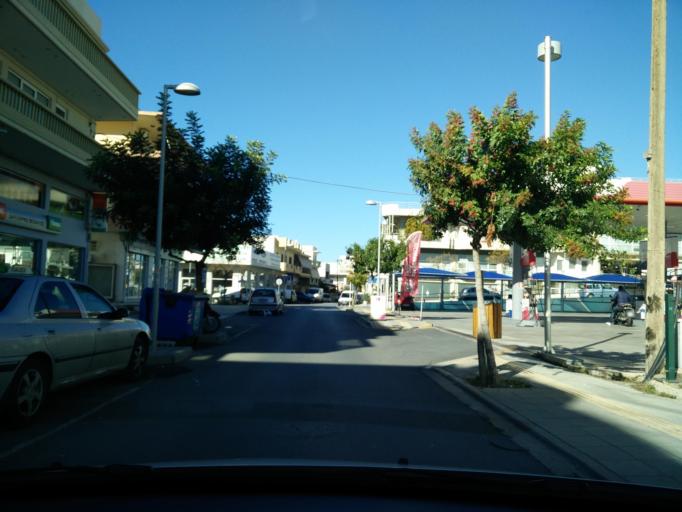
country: GR
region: Crete
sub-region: Nomos Irakleiou
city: Nea Alikarnassos
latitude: 35.3356
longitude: 25.1580
